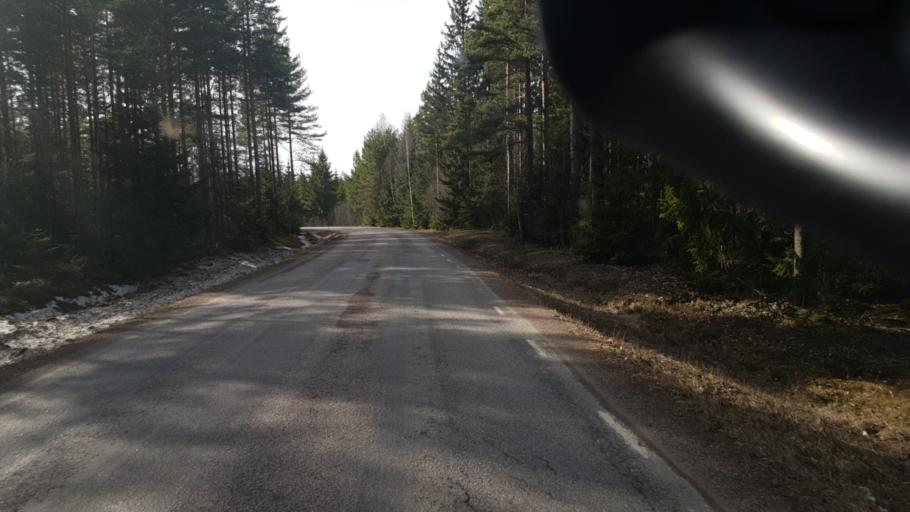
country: SE
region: Vaermland
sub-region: Eda Kommun
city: Charlottenberg
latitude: 59.8523
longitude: 12.3230
